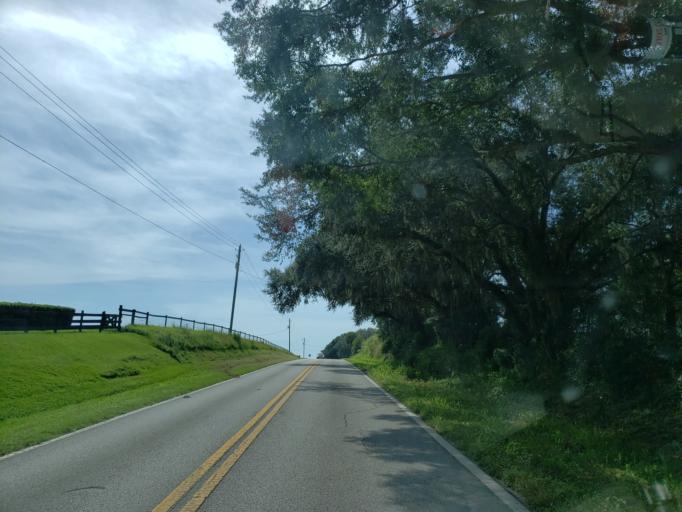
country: US
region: Florida
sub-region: Pasco County
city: San Antonio
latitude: 28.3907
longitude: -82.2915
